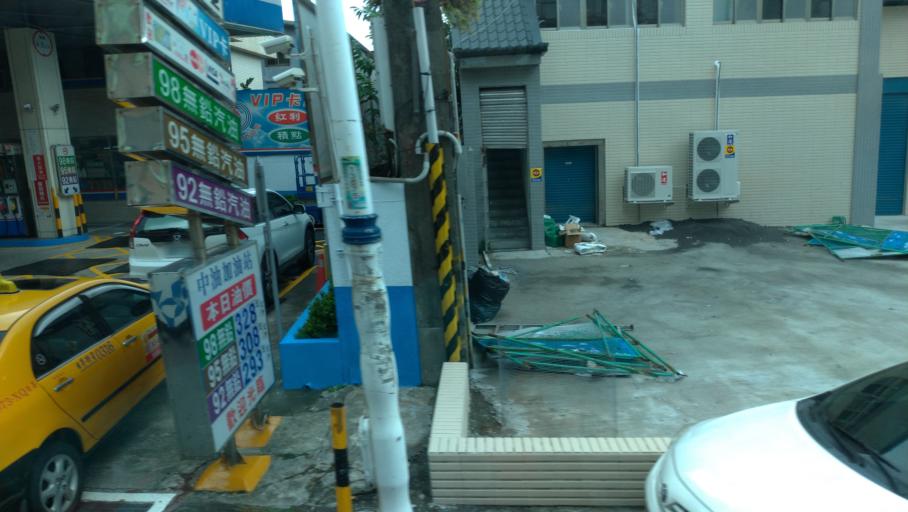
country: TW
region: Taiwan
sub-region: Keelung
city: Keelung
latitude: 25.1517
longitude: 121.7677
